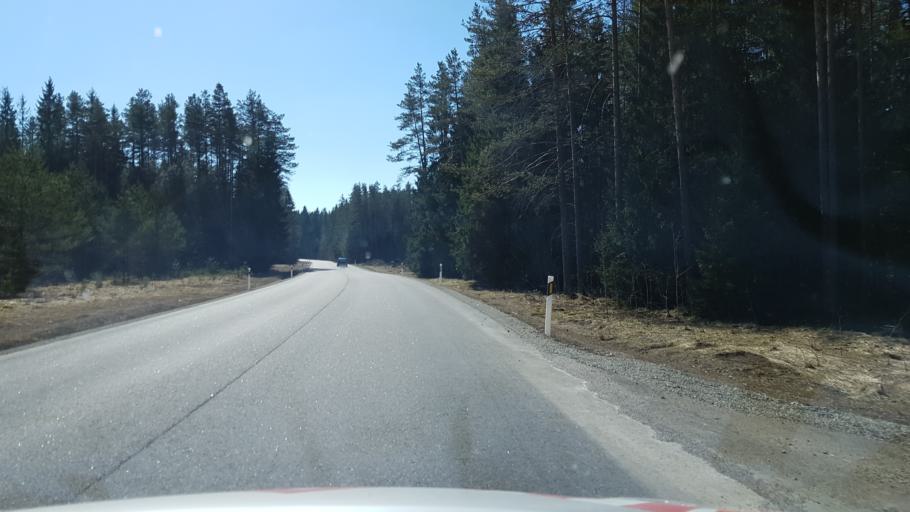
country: EE
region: Laeaene-Virumaa
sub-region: Vinni vald
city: Vinni
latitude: 59.1382
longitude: 26.5977
